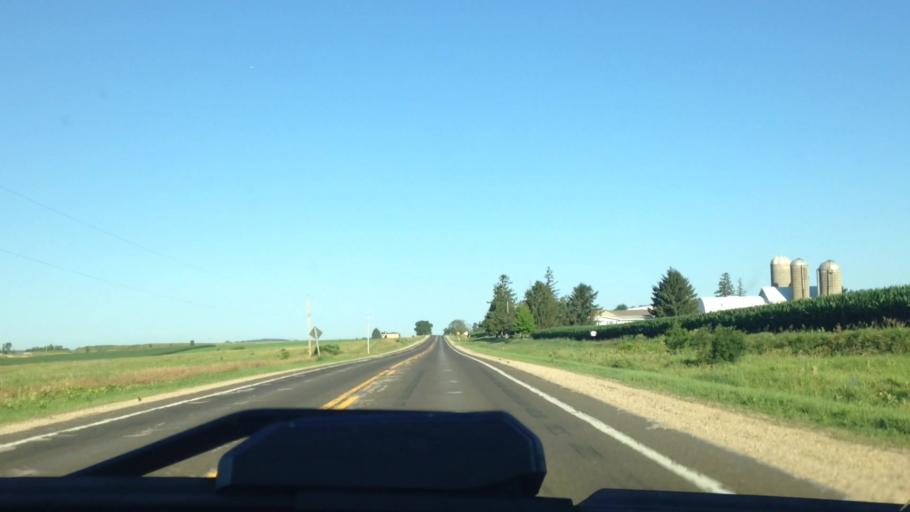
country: US
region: Wisconsin
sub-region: Columbia County
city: Poynette
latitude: 43.3322
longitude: -89.3507
